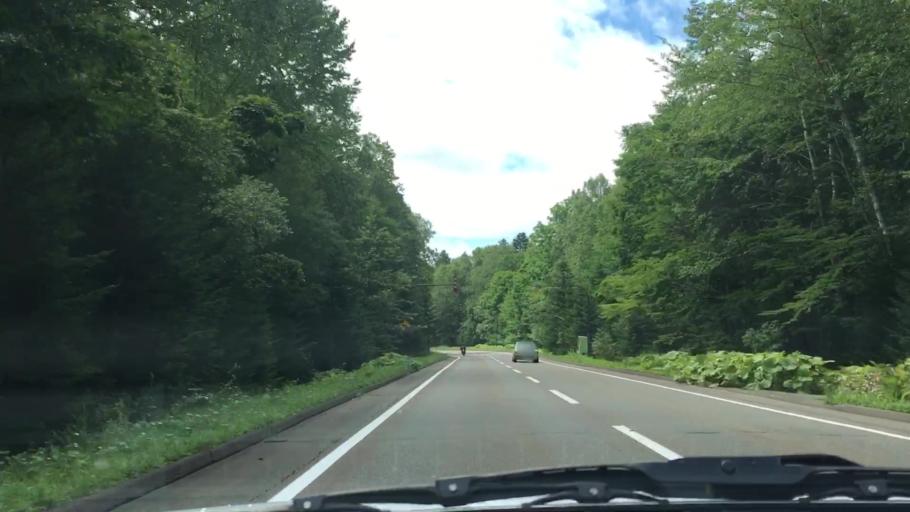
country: JP
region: Hokkaido
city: Kitami
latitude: 43.3995
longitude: 143.9274
